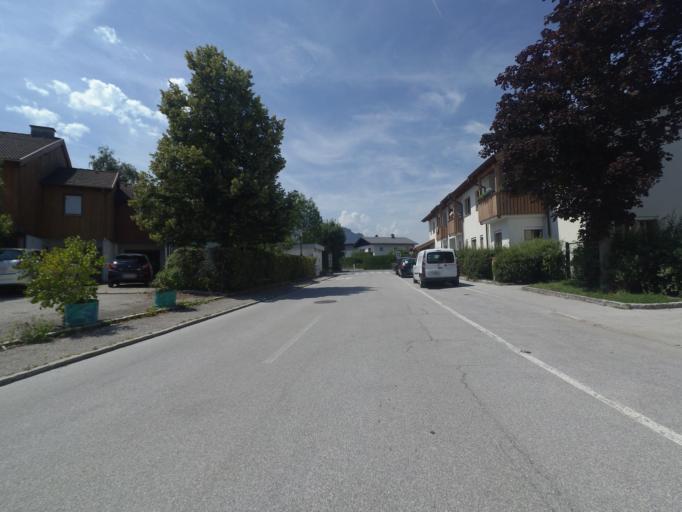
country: AT
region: Salzburg
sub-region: Politischer Bezirk Hallein
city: Puch bei Hallein
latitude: 47.7272
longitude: 13.0774
